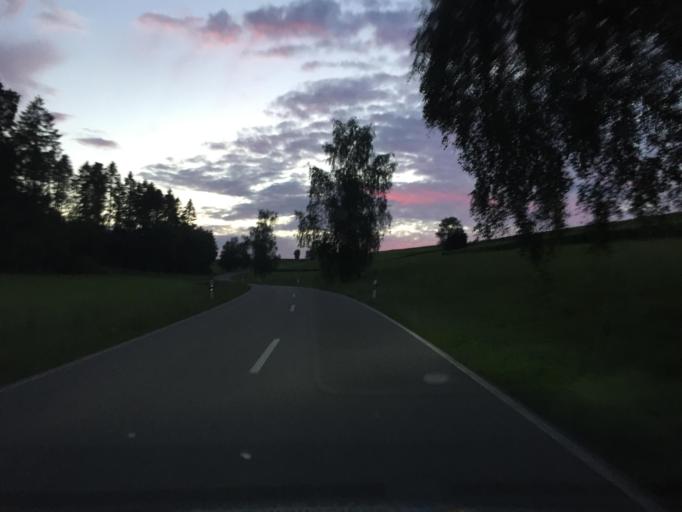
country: DE
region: Baden-Wuerttemberg
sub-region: Freiburg Region
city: Eggingen
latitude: 47.6638
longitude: 8.4137
